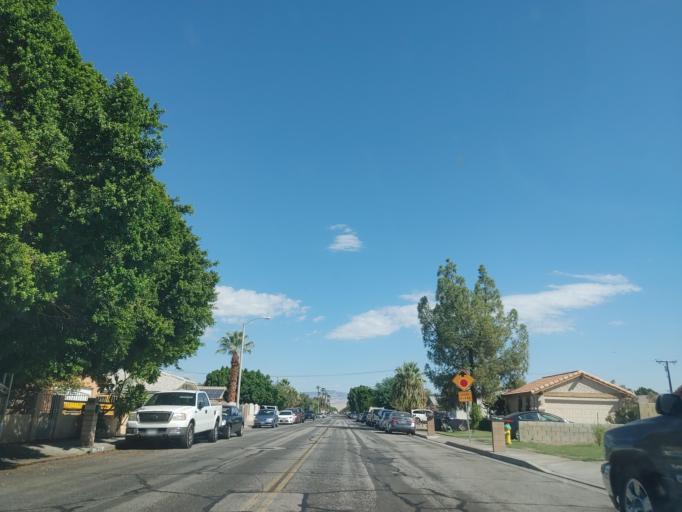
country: US
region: California
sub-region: Riverside County
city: Cathedral City
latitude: 33.8040
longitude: -116.4701
